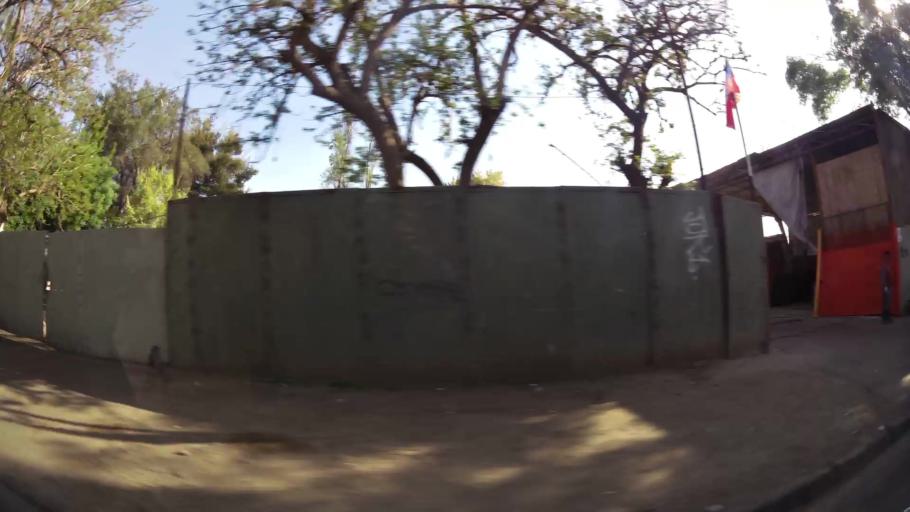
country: CL
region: Santiago Metropolitan
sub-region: Provincia de Santiago
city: Lo Prado
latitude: -33.4136
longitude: -70.7547
